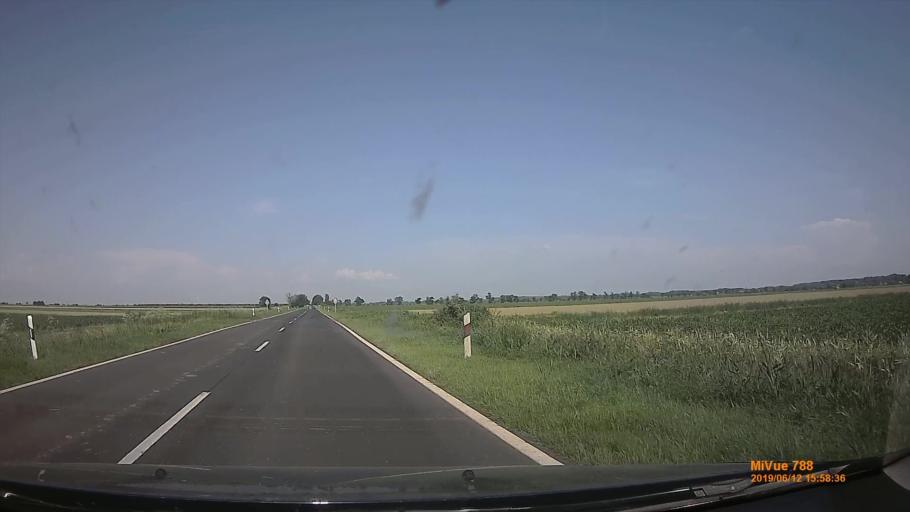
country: HU
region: Csongrad
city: Apatfalva
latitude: 46.1650
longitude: 20.6481
